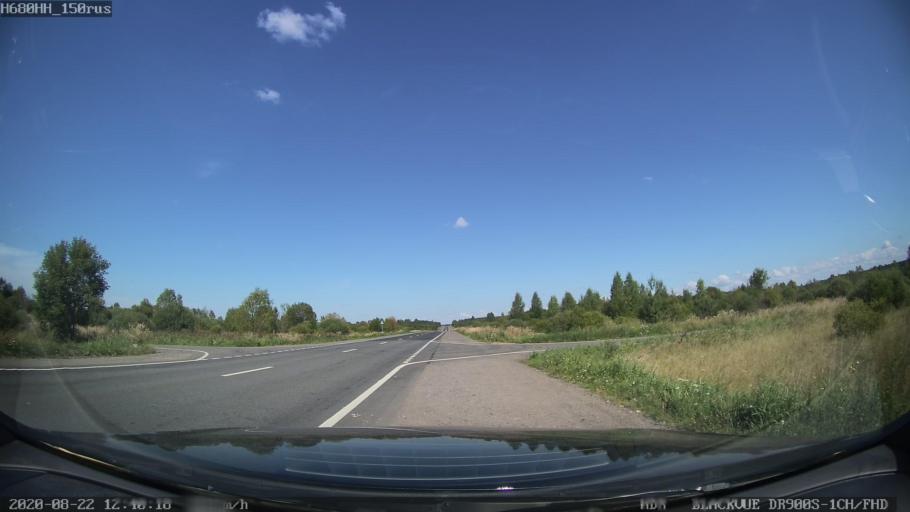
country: RU
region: Tverskaya
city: Rameshki
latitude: 57.3346
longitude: 36.0945
